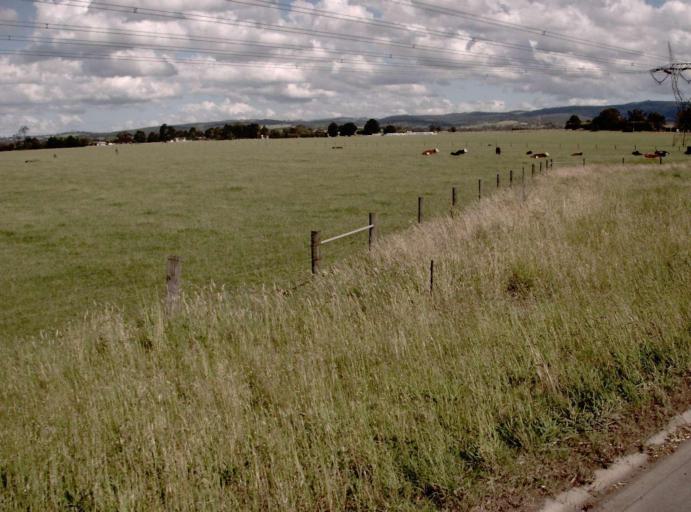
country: AU
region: Victoria
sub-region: Latrobe
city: Morwell
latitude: -38.2627
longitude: 146.4345
